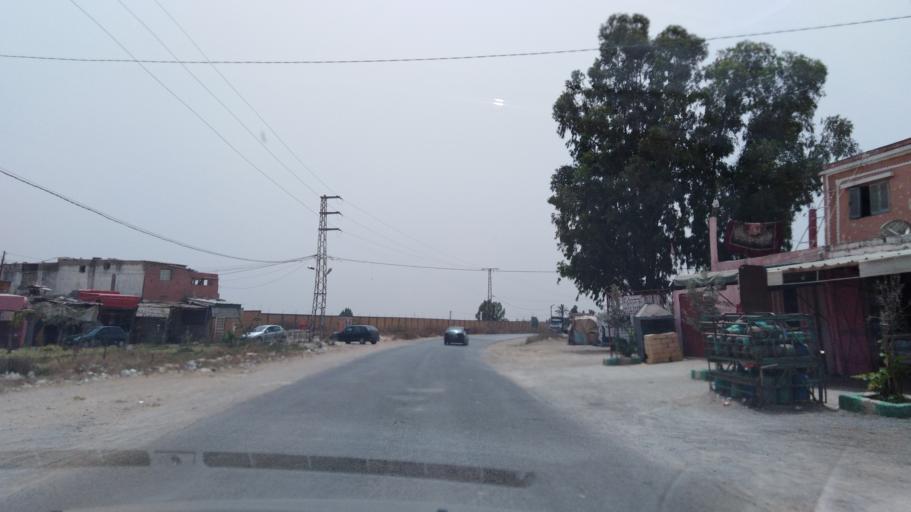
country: MA
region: Grand Casablanca
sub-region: Mediouna
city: Mediouna
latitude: 33.4160
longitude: -7.5170
